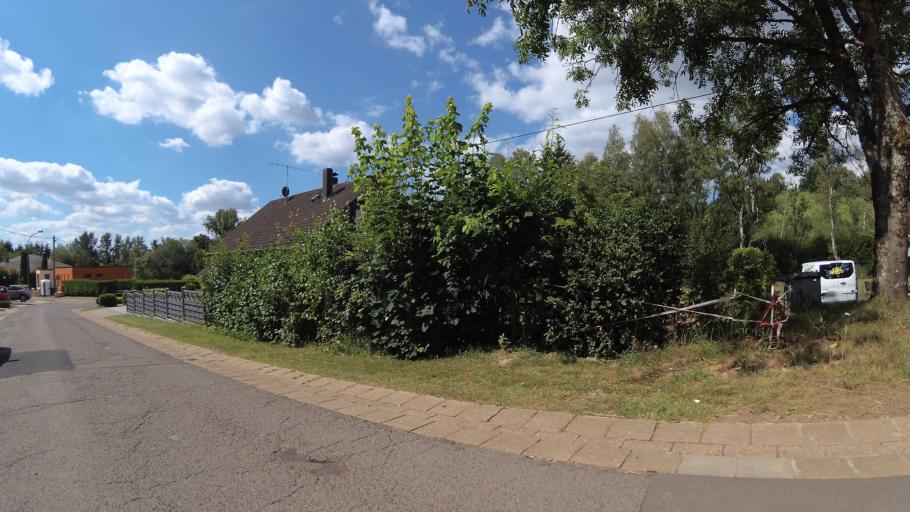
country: DE
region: Saarland
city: Weiskirchen
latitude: 49.5513
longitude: 6.7882
